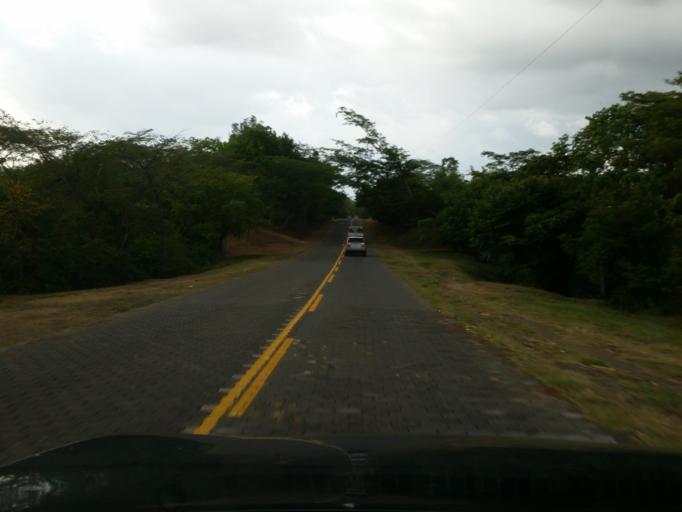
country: NI
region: Managua
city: Carlos Fonseca Amador
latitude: 11.9465
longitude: -86.5092
